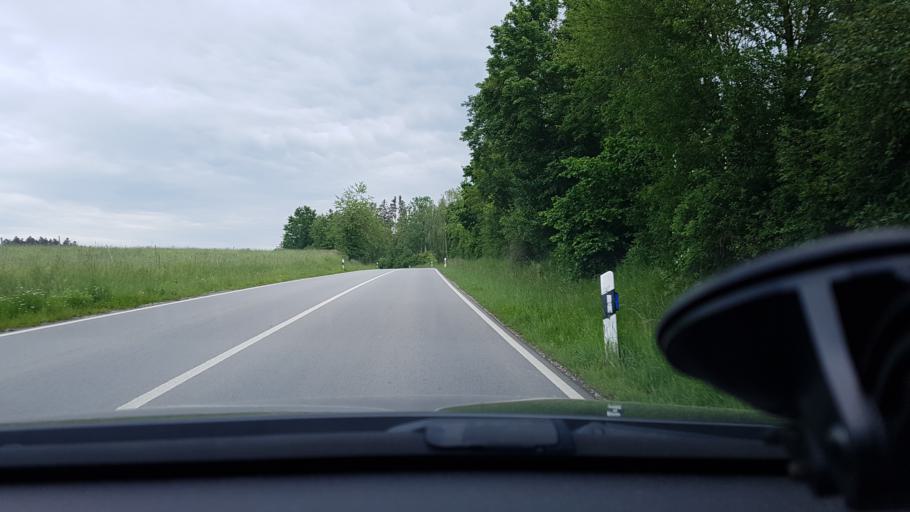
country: DE
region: Bavaria
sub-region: Lower Bavaria
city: Pfarrkirchen
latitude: 48.4118
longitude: 12.9648
